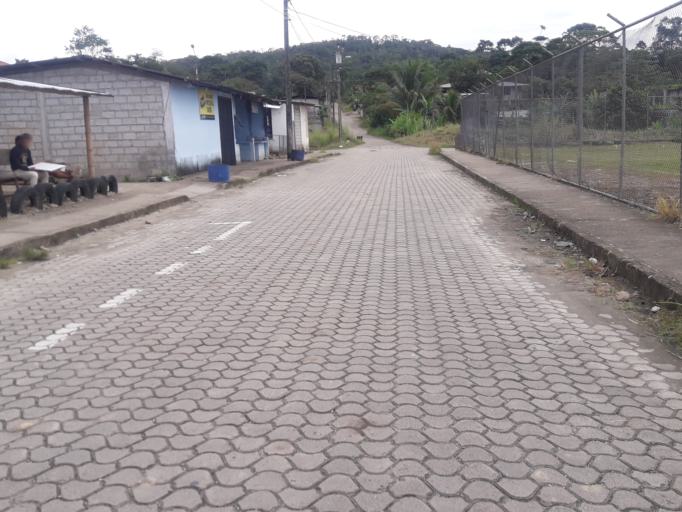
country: EC
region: Napo
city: Tena
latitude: -0.9864
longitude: -77.8297
